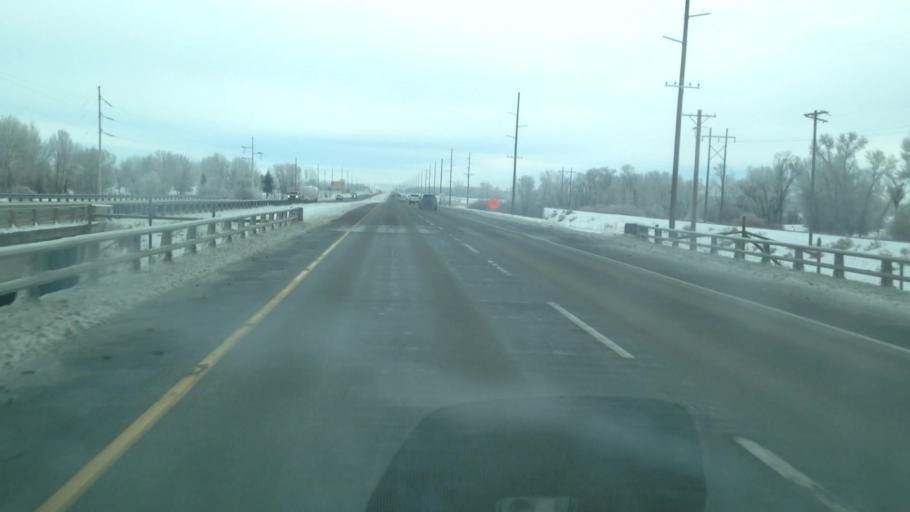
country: US
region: Idaho
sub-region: Jefferson County
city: Rigby
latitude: 43.7322
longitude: -111.8691
